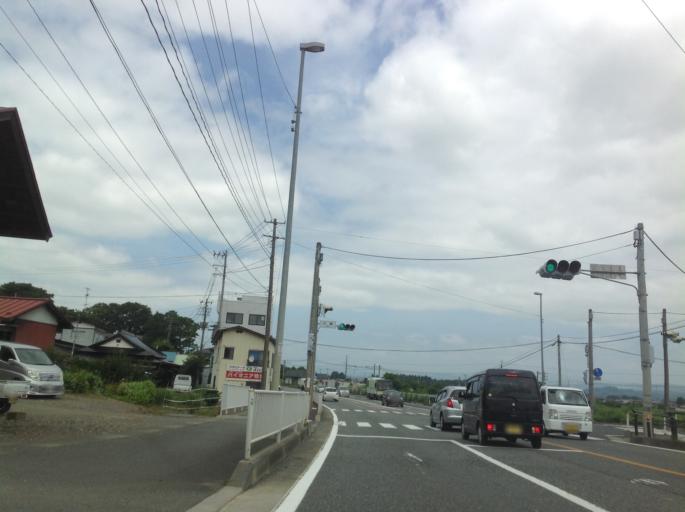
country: JP
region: Iwate
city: Mizusawa
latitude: 39.1156
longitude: 141.1455
